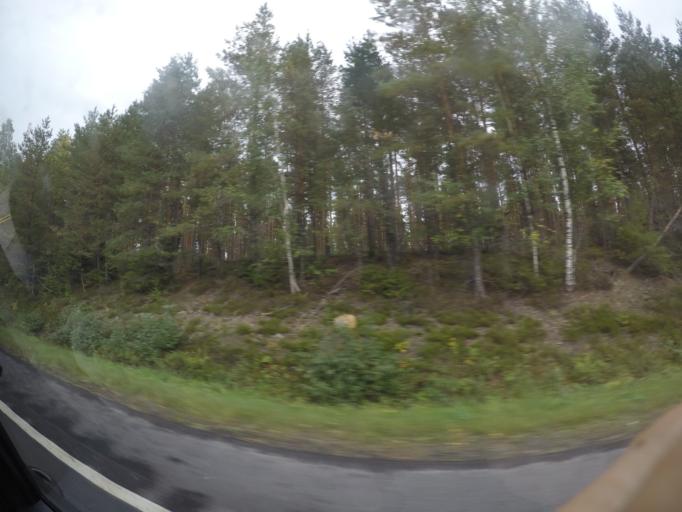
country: FI
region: Haeme
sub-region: Haemeenlinna
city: Parola
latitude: 61.1328
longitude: 24.4176
